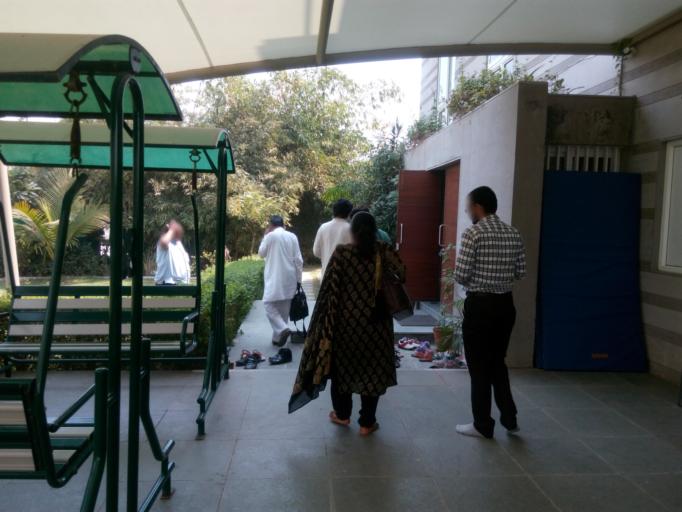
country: IN
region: Gujarat
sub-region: Ahmadabad
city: Sarkhej
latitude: 22.9805
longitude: 72.4753
